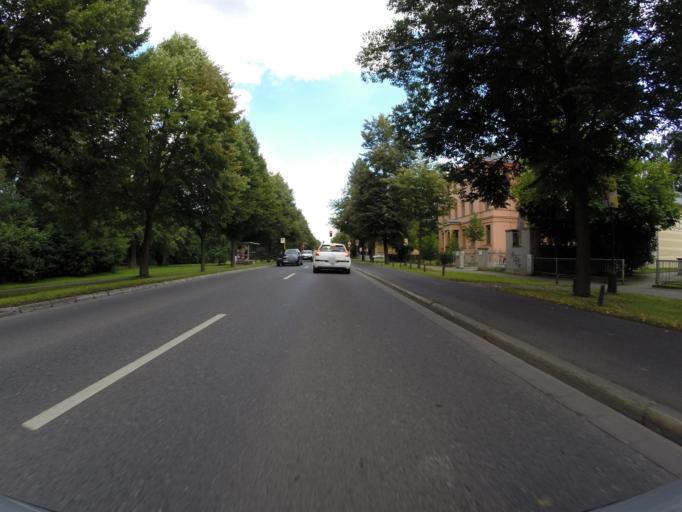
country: DE
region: Thuringia
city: Weimar
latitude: 50.9737
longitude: 11.3309
